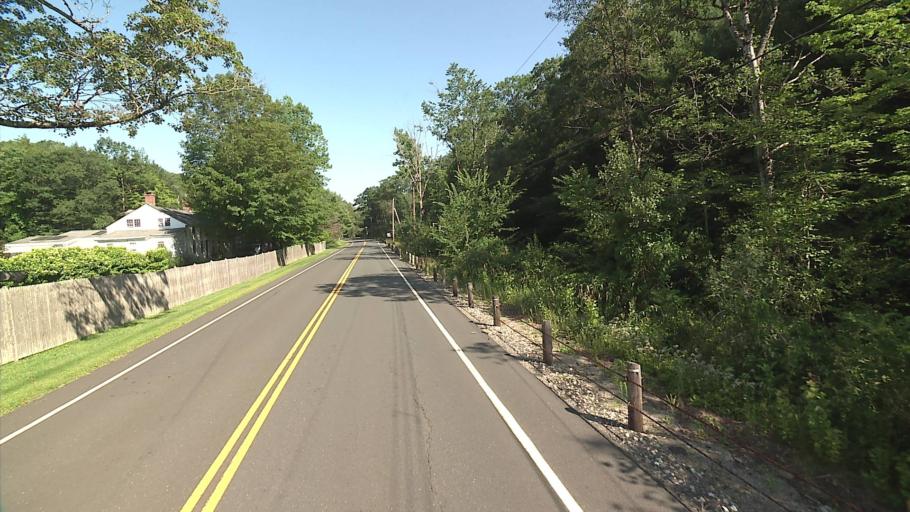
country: US
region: Massachusetts
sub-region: Berkshire County
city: New Marlborough
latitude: 42.0395
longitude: -73.1316
